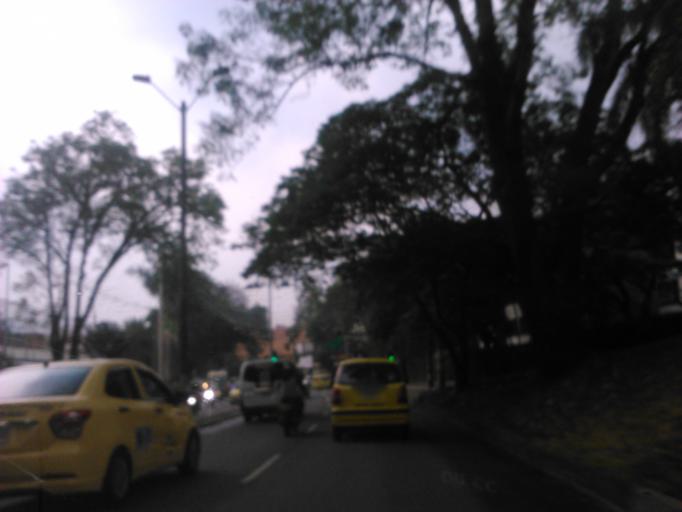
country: CO
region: Antioquia
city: Medellin
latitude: 6.2538
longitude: -75.5993
